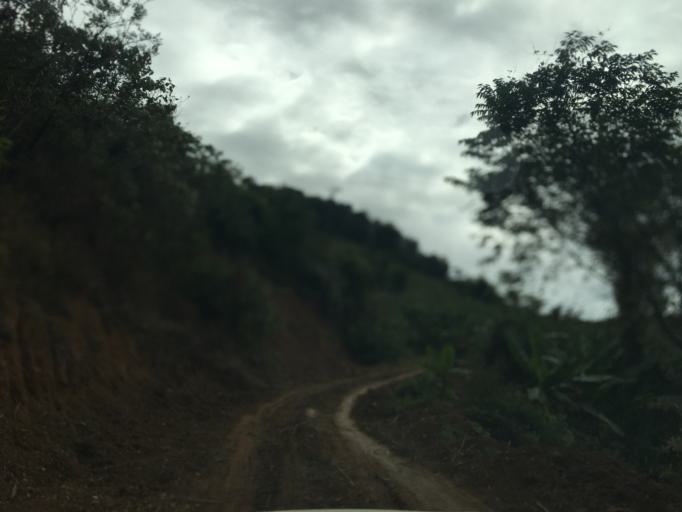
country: LA
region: Houaphan
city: Viengthong
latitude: 19.9198
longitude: 103.2980
